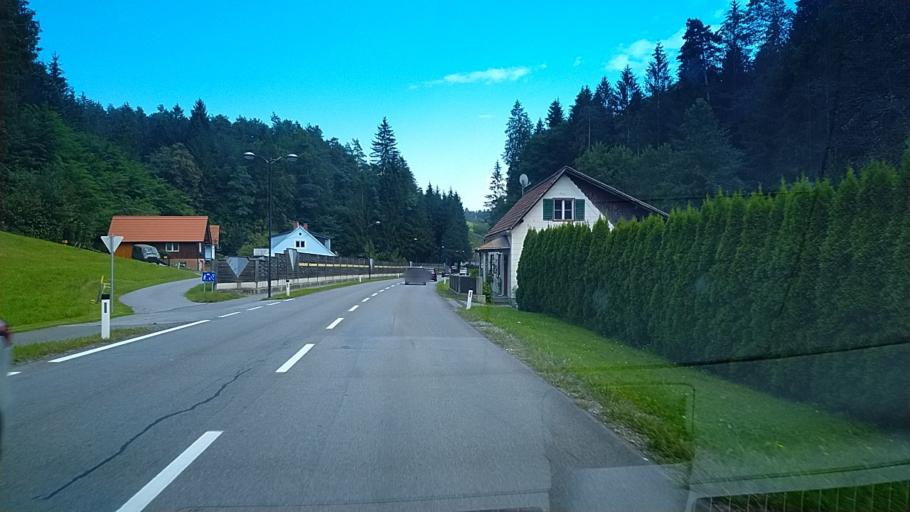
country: AT
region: Styria
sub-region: Politischer Bezirk Deutschlandsberg
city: Sankt Peter im Sulmtal
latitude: 46.7340
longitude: 15.2438
